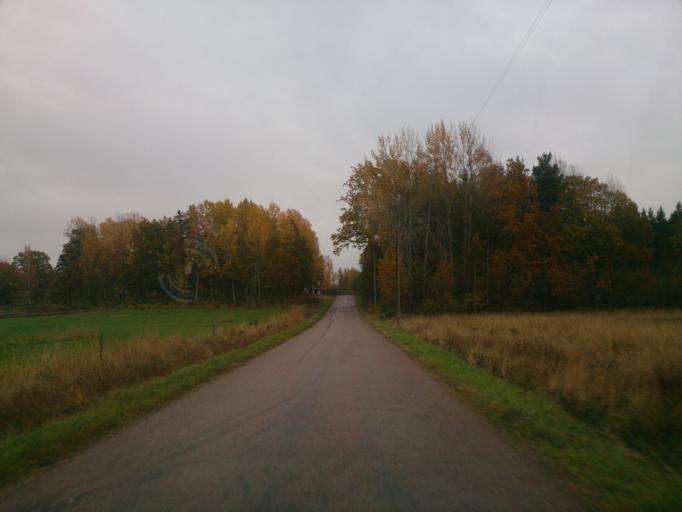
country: SE
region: OEstergoetland
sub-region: Atvidabergs Kommun
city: Atvidaberg
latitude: 58.3298
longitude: 16.0240
